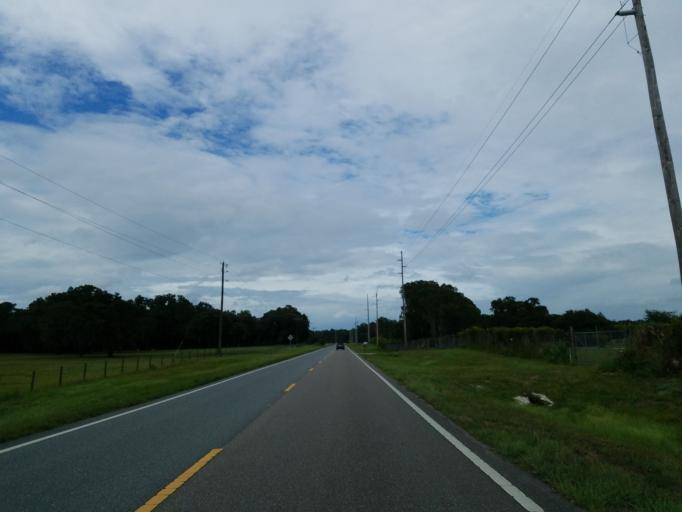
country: US
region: Florida
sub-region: Sumter County
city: Lake Panasoffkee
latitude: 28.8356
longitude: -82.1769
